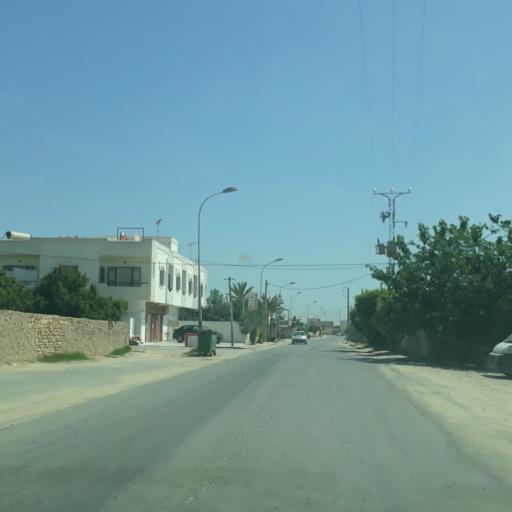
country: TN
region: Safaqis
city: Al Qarmadah
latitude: 34.8119
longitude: 10.7667
